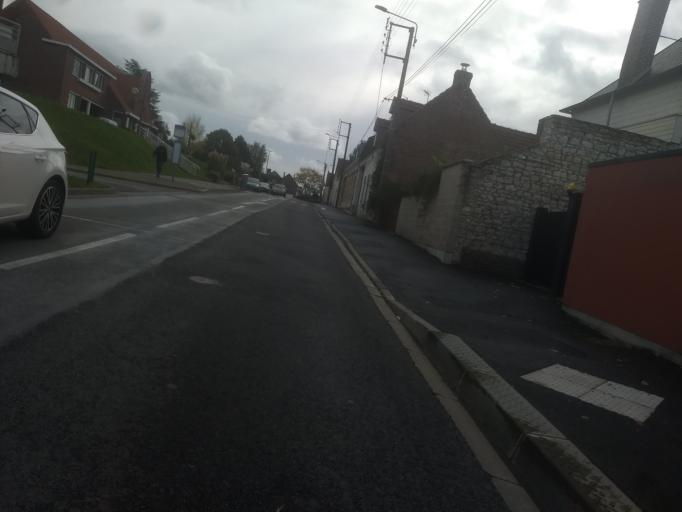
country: FR
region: Nord-Pas-de-Calais
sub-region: Departement du Pas-de-Calais
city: Anzin-Saint-Aubin
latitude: 50.3113
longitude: 2.7491
